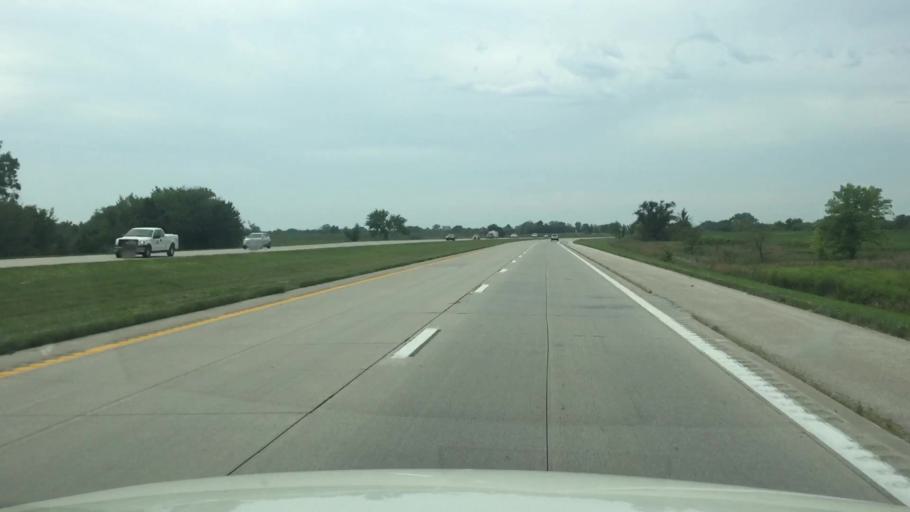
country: US
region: Missouri
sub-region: Daviess County
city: Gallatin
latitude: 39.9564
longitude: -94.1064
